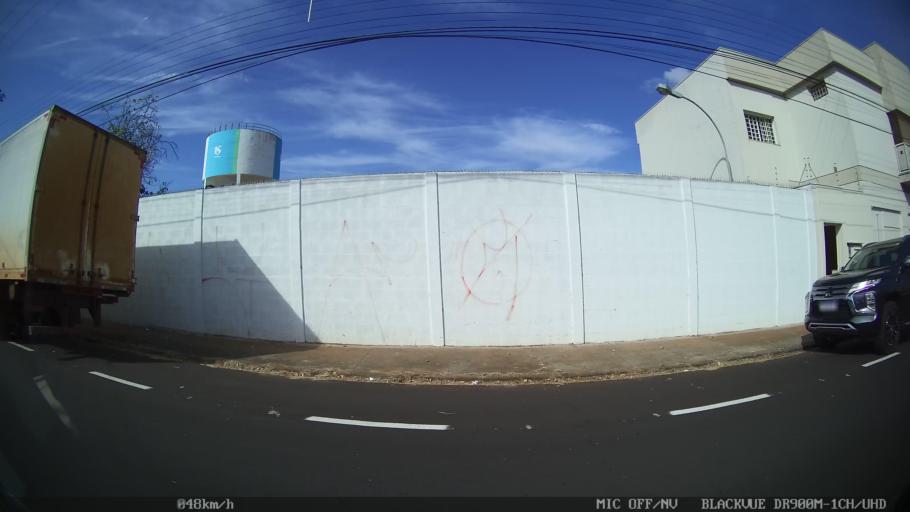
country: BR
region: Sao Paulo
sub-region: Franca
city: Franca
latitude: -20.5341
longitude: -47.4167
